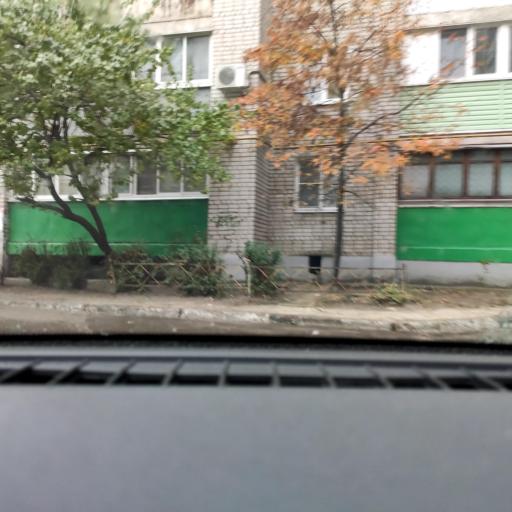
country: RU
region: Voronezj
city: Maslovka
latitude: 51.5969
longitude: 39.2427
